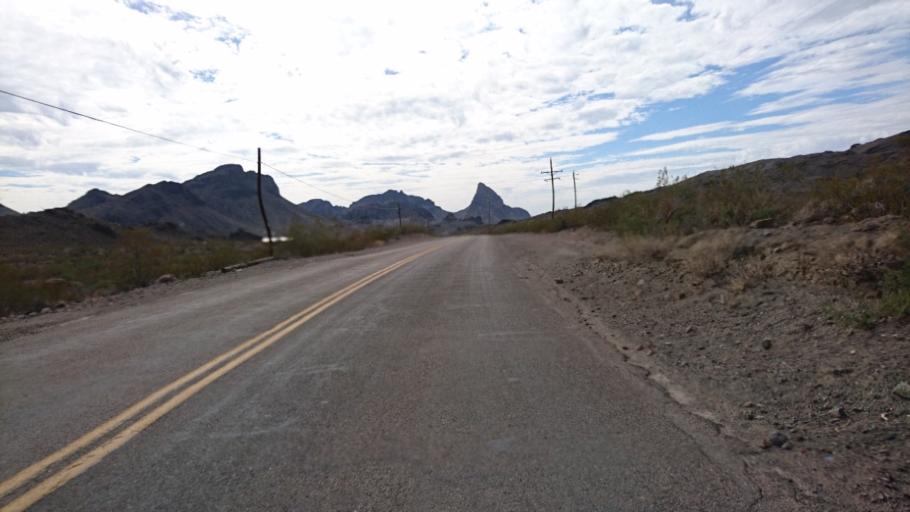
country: US
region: Arizona
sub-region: Mohave County
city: Mohave Valley
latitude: 35.0173
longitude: -114.3854
